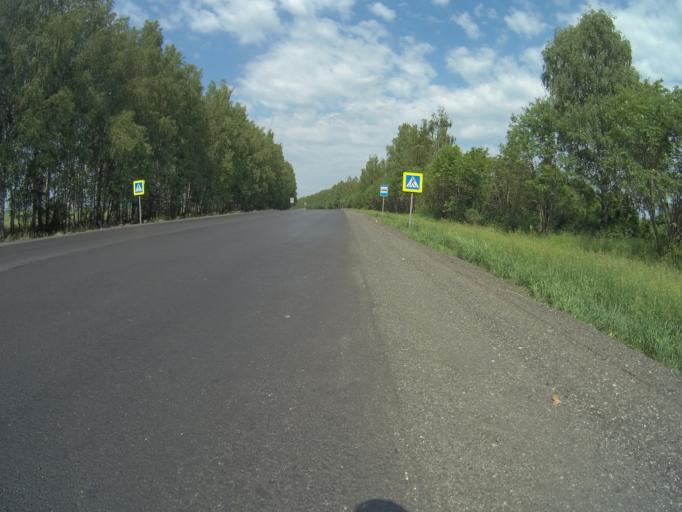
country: RU
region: Vladimir
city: Bogolyubovo
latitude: 56.2584
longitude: 40.4629
